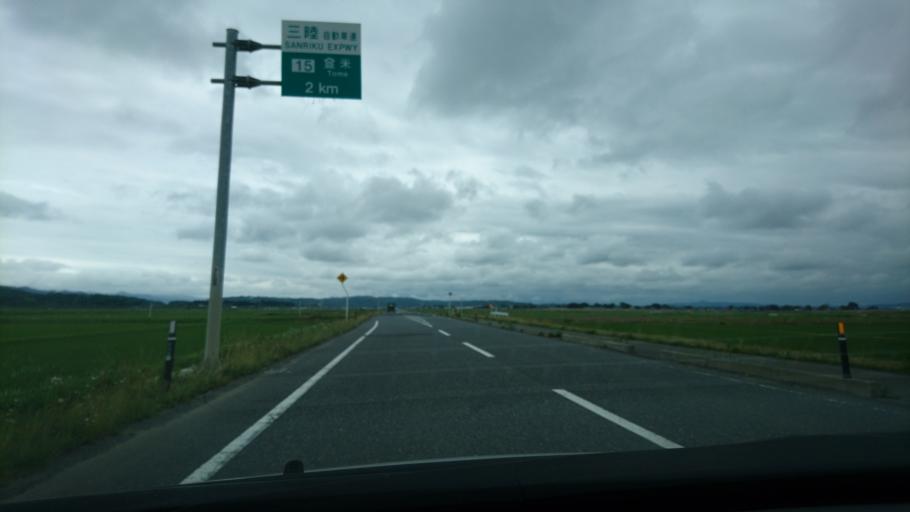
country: JP
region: Miyagi
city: Wakuya
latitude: 38.6909
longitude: 141.2607
